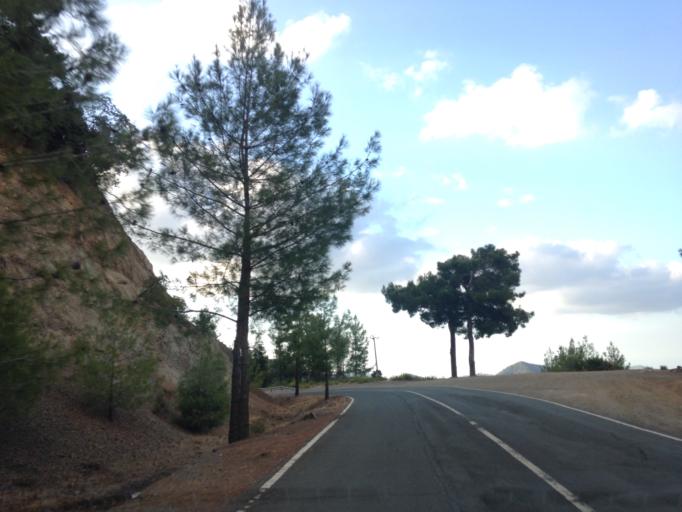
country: CY
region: Lefkosia
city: Kakopetria
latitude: 34.9857
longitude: 32.7441
